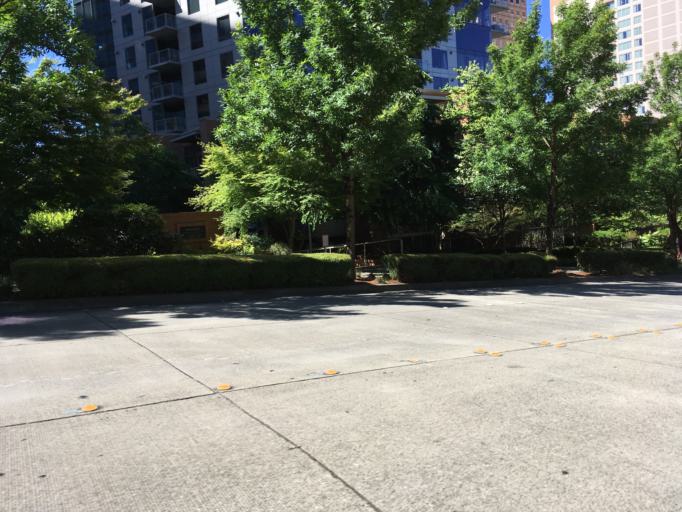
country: US
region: Washington
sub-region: King County
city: Bellevue
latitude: 47.6193
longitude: -122.1979
